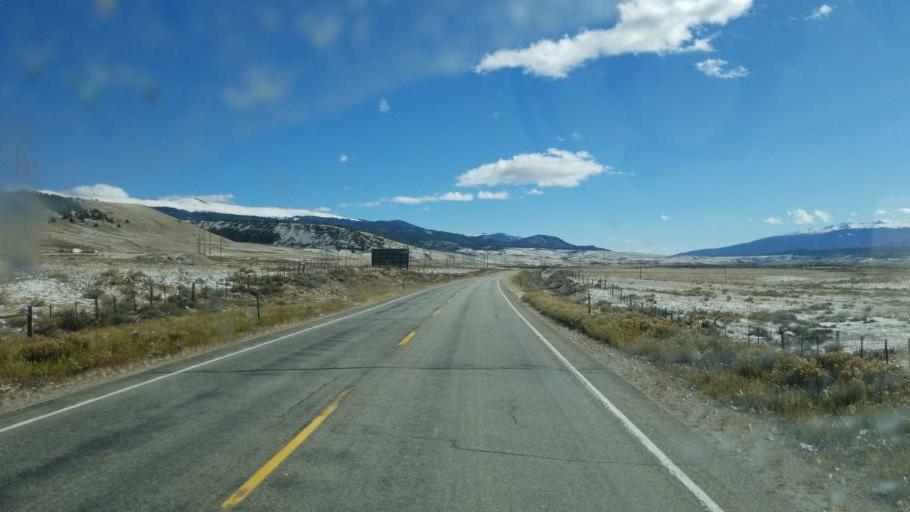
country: US
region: Colorado
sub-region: Lake County
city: Leadville
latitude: 39.1877
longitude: -106.3299
